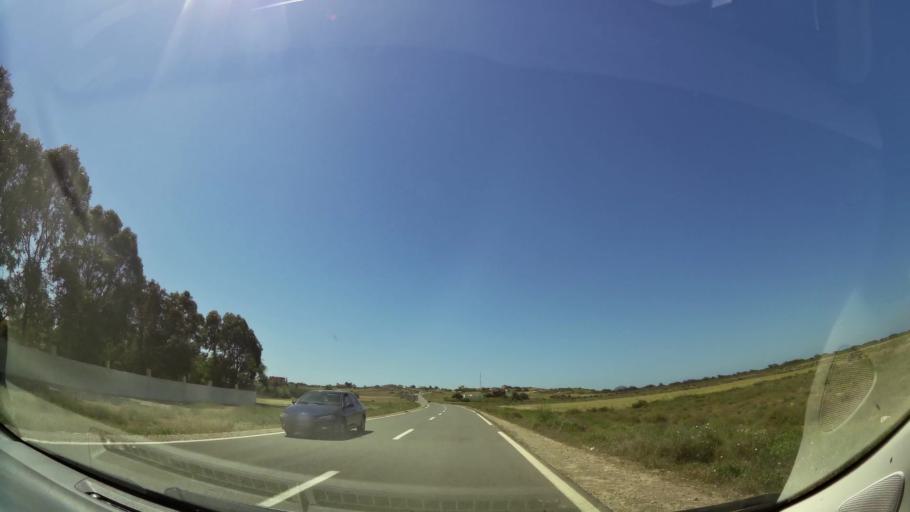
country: MA
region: Oriental
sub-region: Berkane-Taourirt
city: Madagh
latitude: 35.1192
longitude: -2.3739
